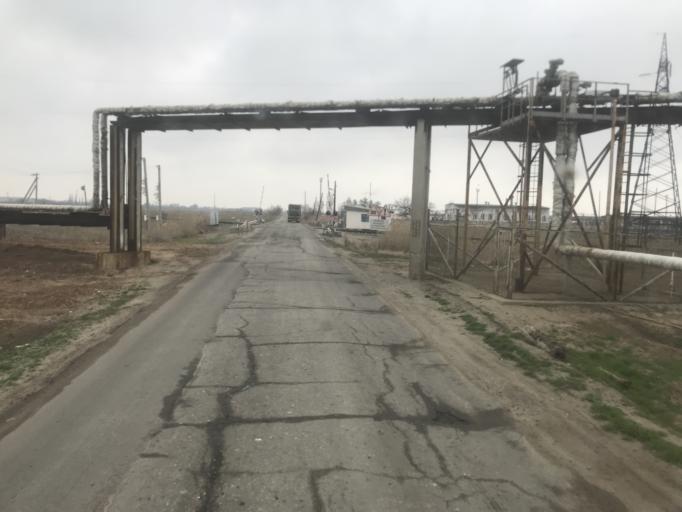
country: RU
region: Volgograd
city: Svetlyy Yar
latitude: 48.5136
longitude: 44.6342
